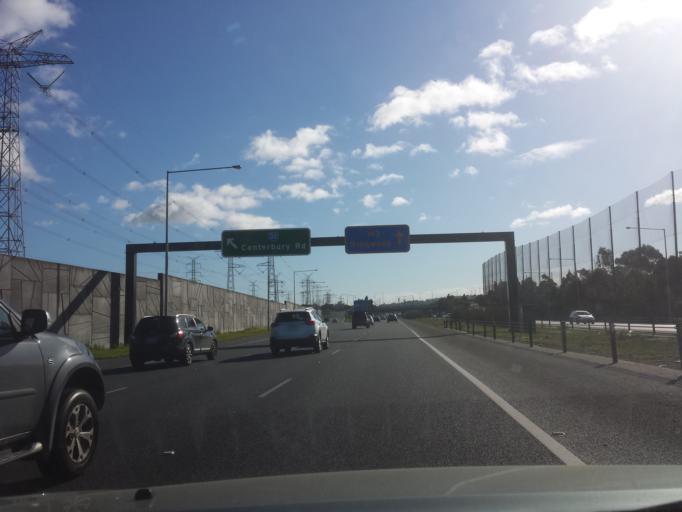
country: AU
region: Victoria
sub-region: Knox
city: Wantirna
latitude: -37.8372
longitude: 145.2176
